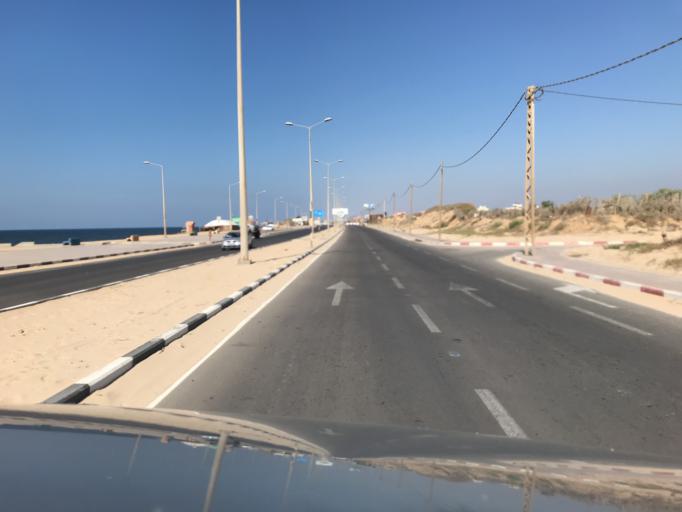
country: PS
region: Gaza Strip
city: An Nusayrat
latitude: 31.4738
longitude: 34.3859
